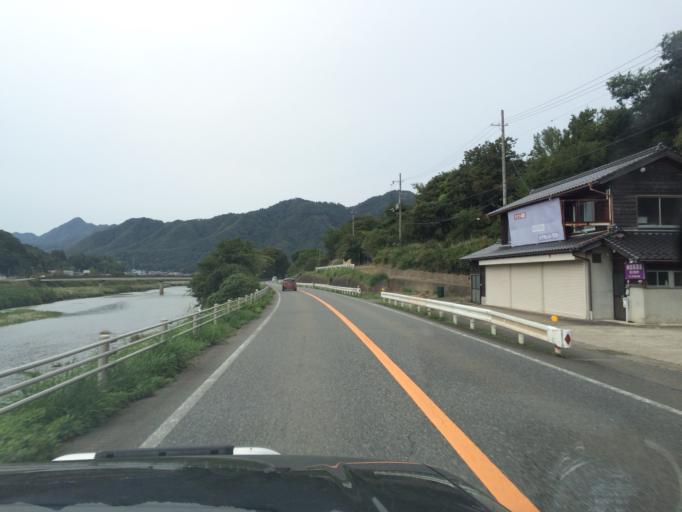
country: JP
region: Hyogo
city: Toyooka
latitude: 35.3978
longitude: 134.7885
